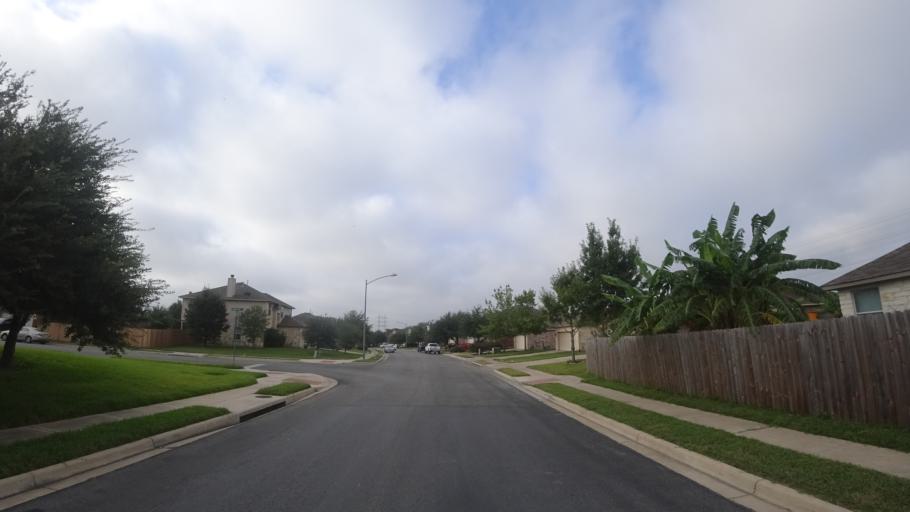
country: US
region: Texas
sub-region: Travis County
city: Pflugerville
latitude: 30.3582
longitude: -97.6451
